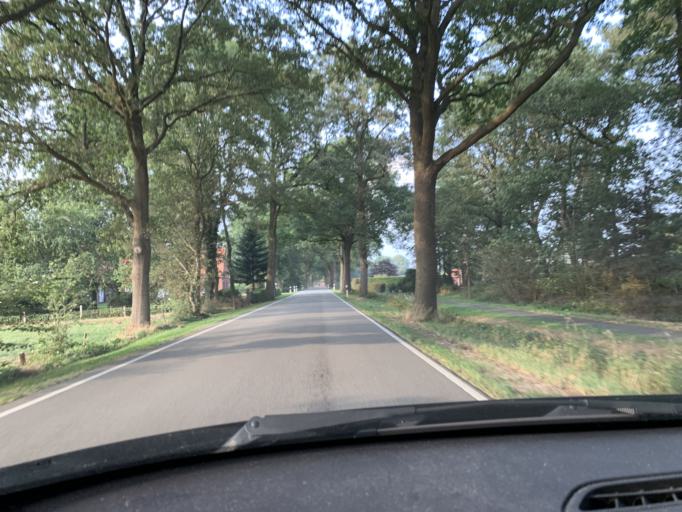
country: DE
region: Lower Saxony
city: Apen
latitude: 53.1855
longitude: 7.7822
